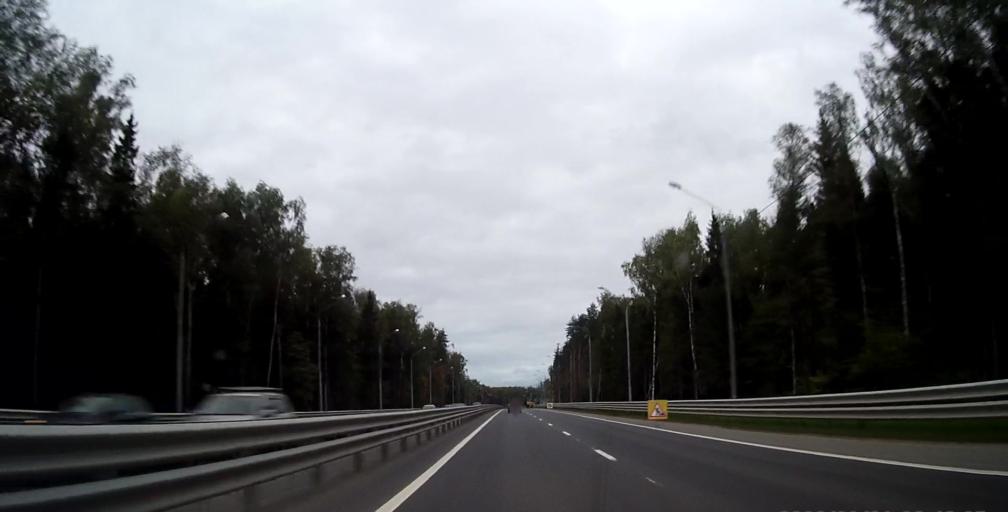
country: RU
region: Moskovskaya
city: Klimovsk
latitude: 55.3852
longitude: 37.5170
